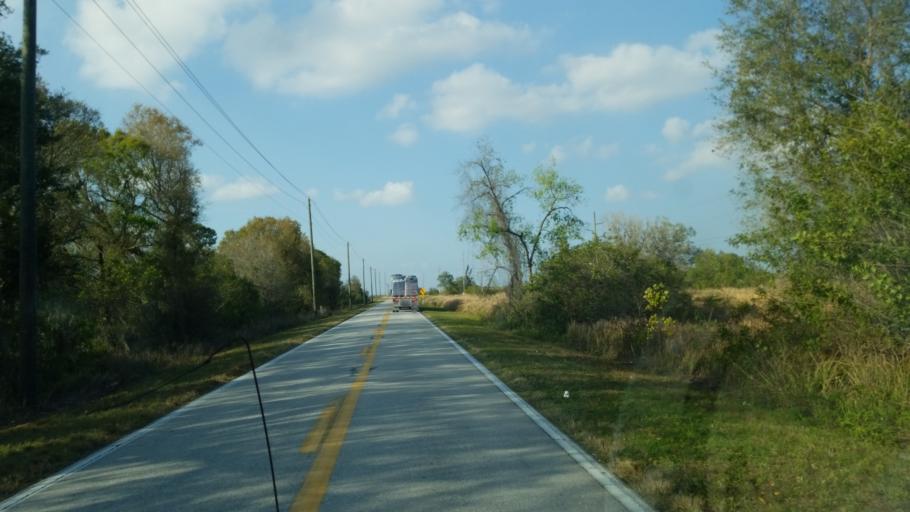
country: US
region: Florida
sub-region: Hardee County
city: Bowling Green
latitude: 27.6957
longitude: -81.9573
